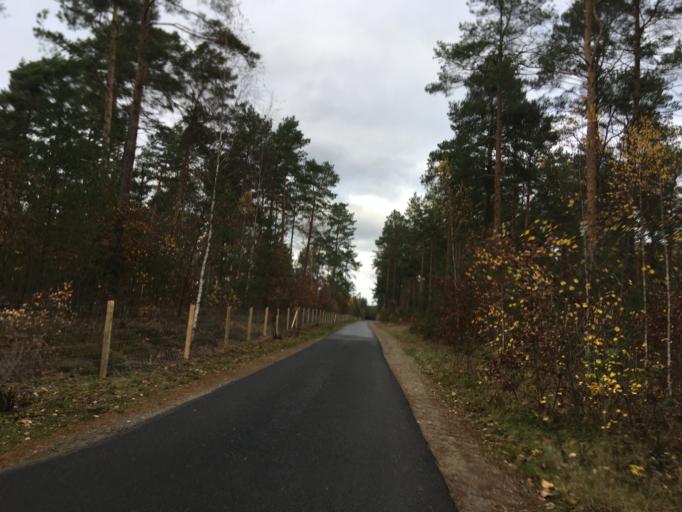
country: DE
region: Brandenburg
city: Tauer
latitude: 51.9897
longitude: 14.5162
